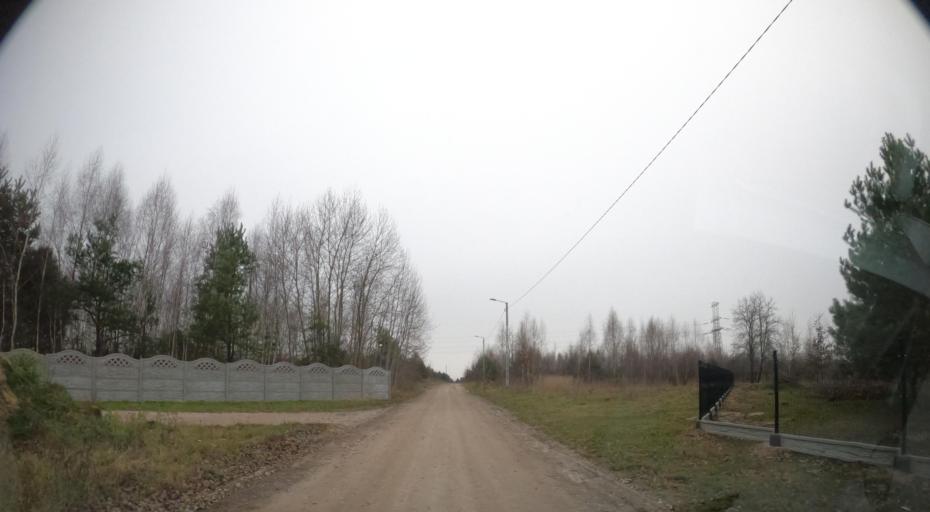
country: PL
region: Masovian Voivodeship
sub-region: Powiat radomski
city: Jastrzebia
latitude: 51.4835
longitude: 21.1910
